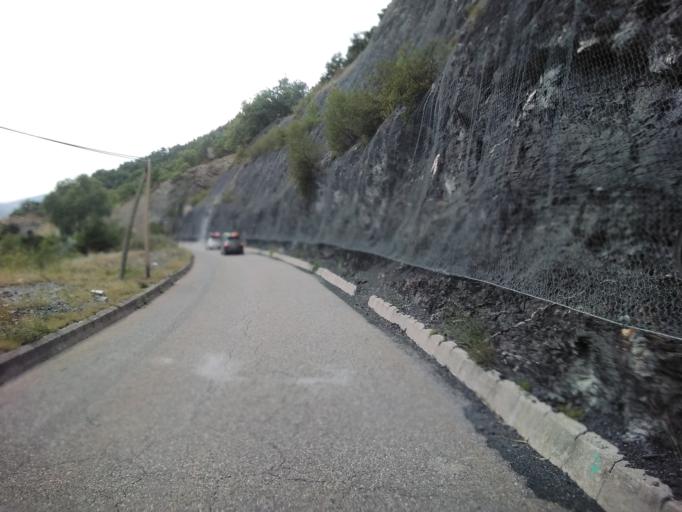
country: FR
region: Provence-Alpes-Cote d'Azur
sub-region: Departement des Alpes-de-Haute-Provence
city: Seyne-les-Alpes
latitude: 44.4568
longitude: 6.3856
